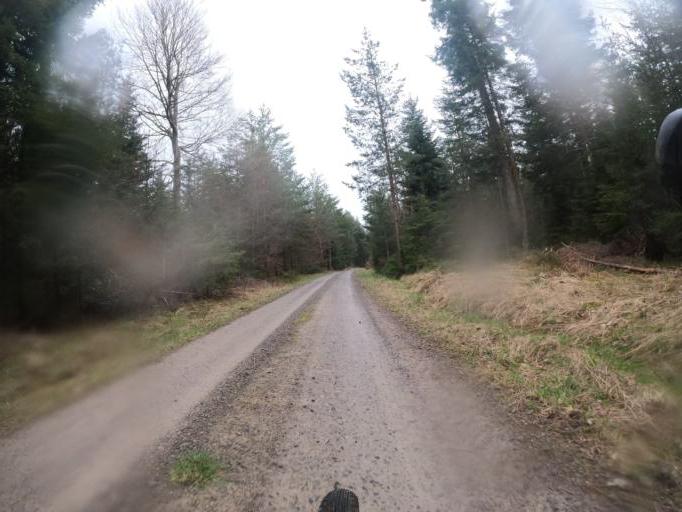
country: DE
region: Baden-Wuerttemberg
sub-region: Karlsruhe Region
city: Neuweiler
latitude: 48.6904
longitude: 8.6035
